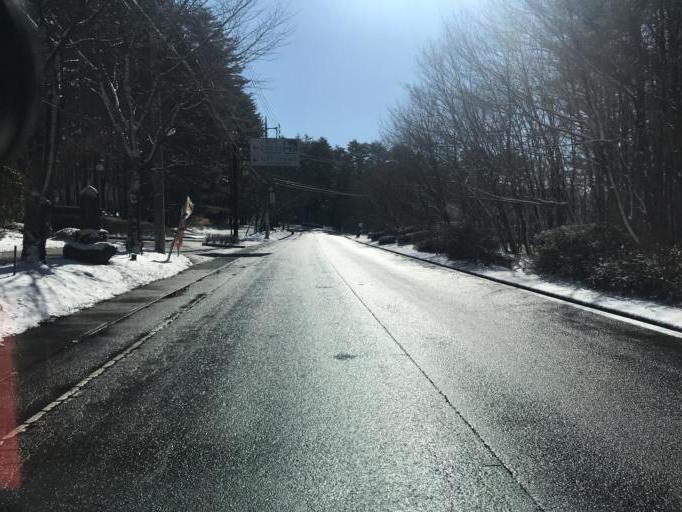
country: JP
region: Nagano
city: Chino
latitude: 35.8782
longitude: 138.3170
